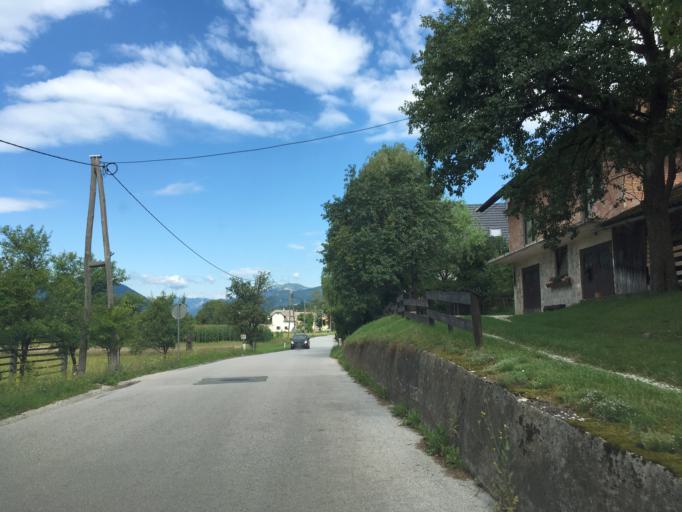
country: SI
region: Zirovnica
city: Zirovnica
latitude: 46.3901
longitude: 14.1647
